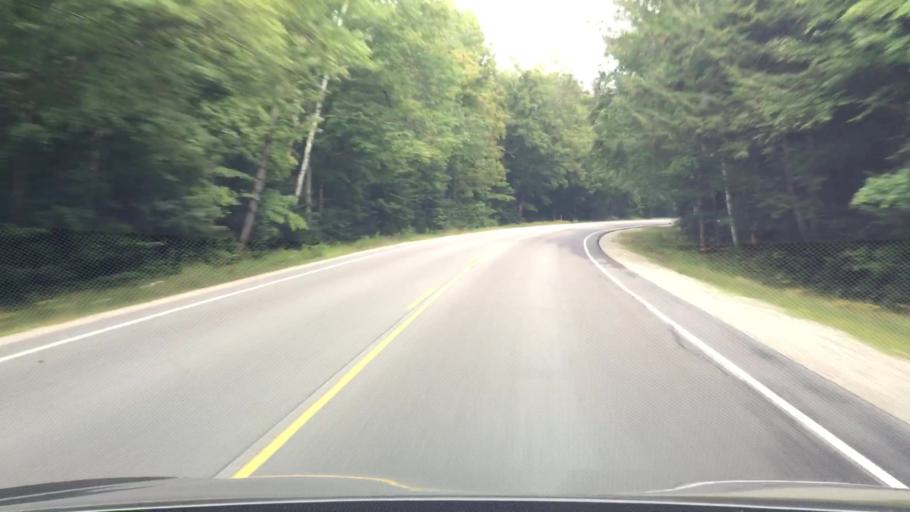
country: US
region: New Hampshire
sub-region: Carroll County
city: Tamworth
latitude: 43.9974
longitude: -71.3840
